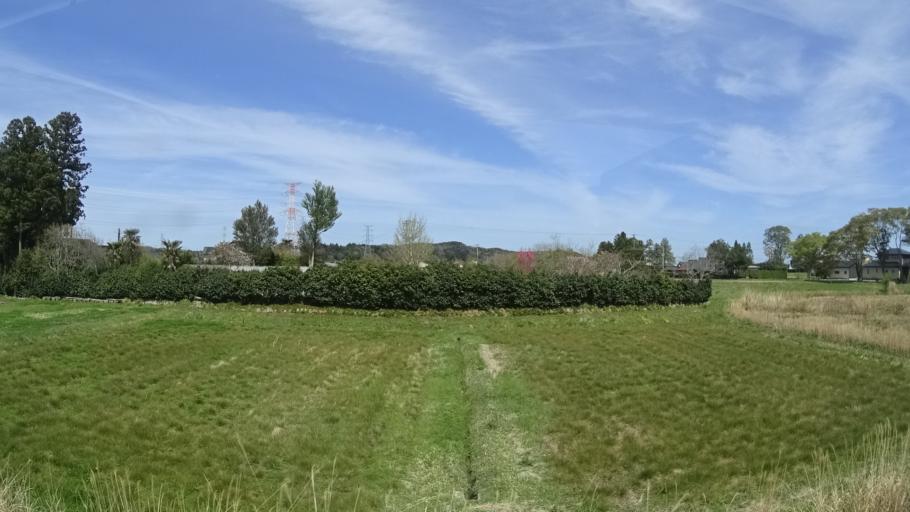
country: JP
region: Fukushima
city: Namie
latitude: 37.5936
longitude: 140.9991
